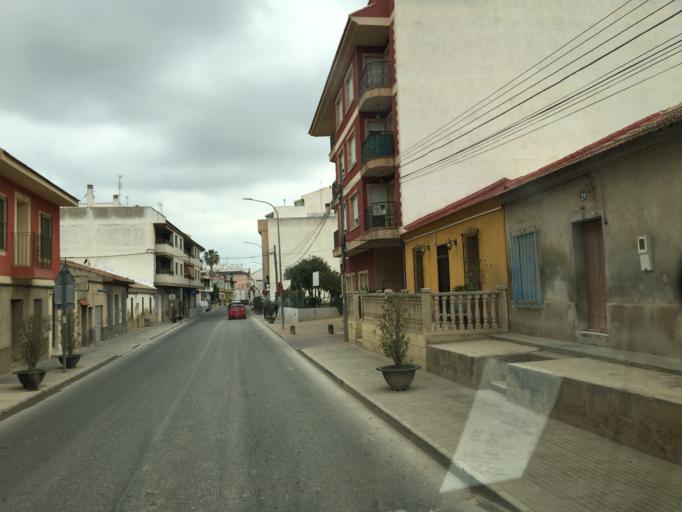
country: ES
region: Murcia
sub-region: Murcia
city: Beniel
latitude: 38.0096
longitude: -0.9999
